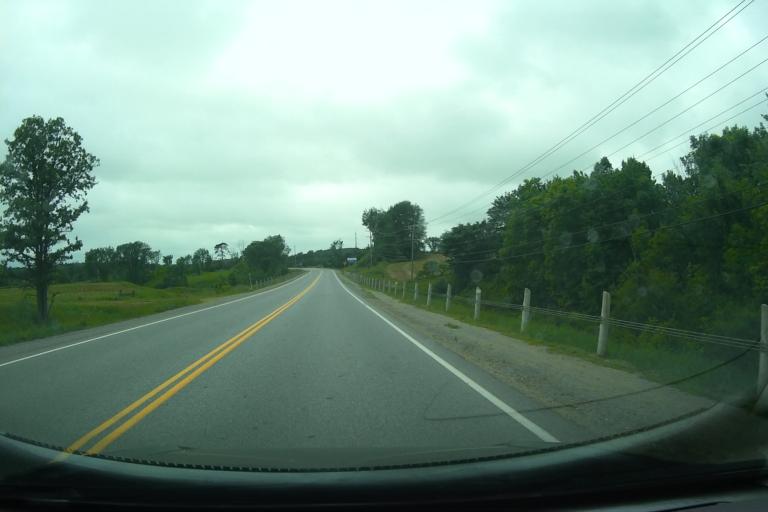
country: CA
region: Ontario
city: Renfrew
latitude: 45.5066
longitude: -76.7557
